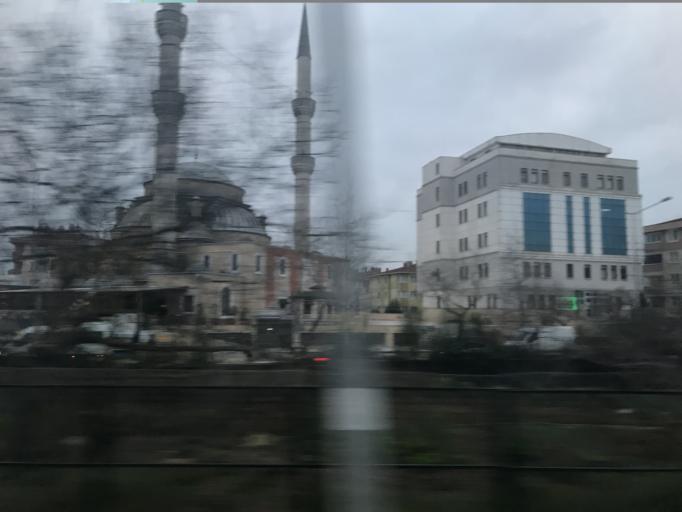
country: TR
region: Istanbul
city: Icmeler
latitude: 40.8412
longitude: 29.3062
